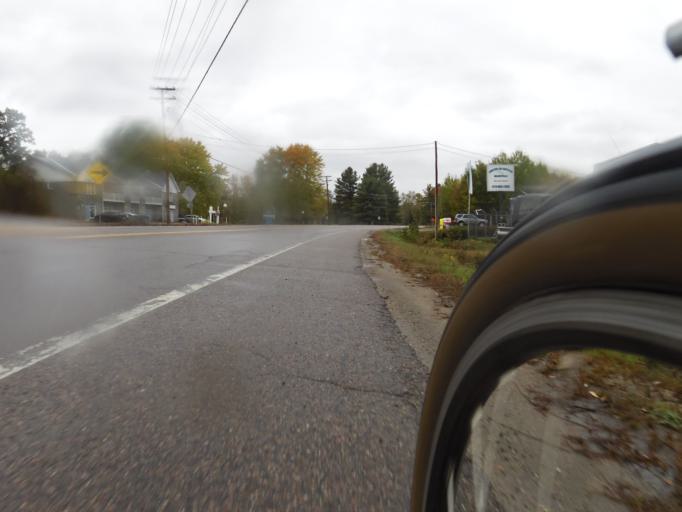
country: CA
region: Quebec
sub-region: Outaouais
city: Fort-Coulonge
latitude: 45.8548
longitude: -76.7380
